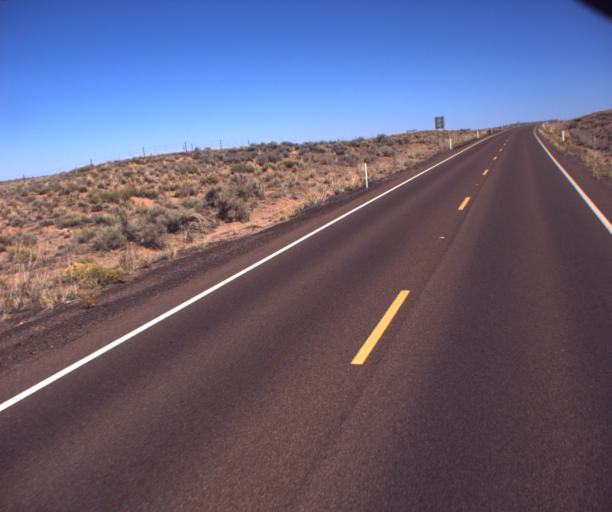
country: US
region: Arizona
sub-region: Navajo County
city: Winslow
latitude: 35.0172
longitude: -110.6357
